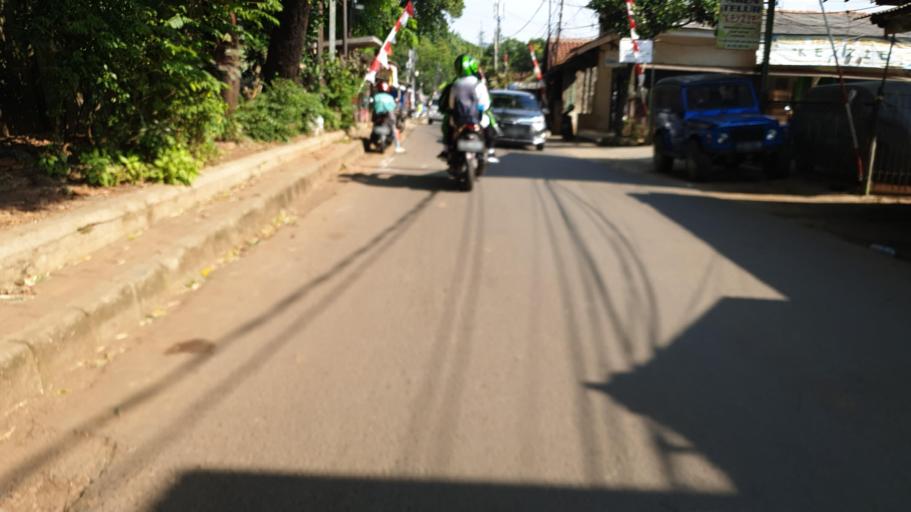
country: ID
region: Jakarta Raya
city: Jakarta
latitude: -6.2904
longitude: 106.8365
